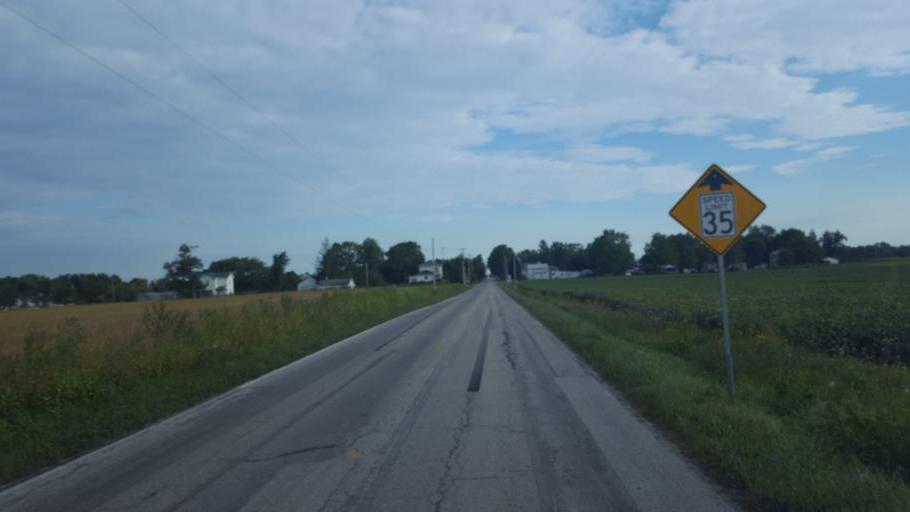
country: US
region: Ohio
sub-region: Crawford County
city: Galion
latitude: 40.6642
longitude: -82.9100
